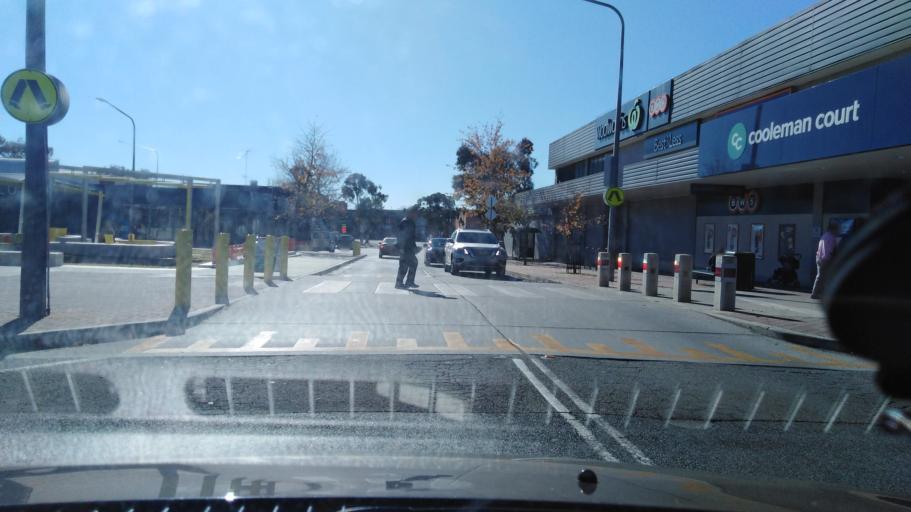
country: AU
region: Australian Capital Territory
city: Forrest
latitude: -35.3415
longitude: 149.0523
